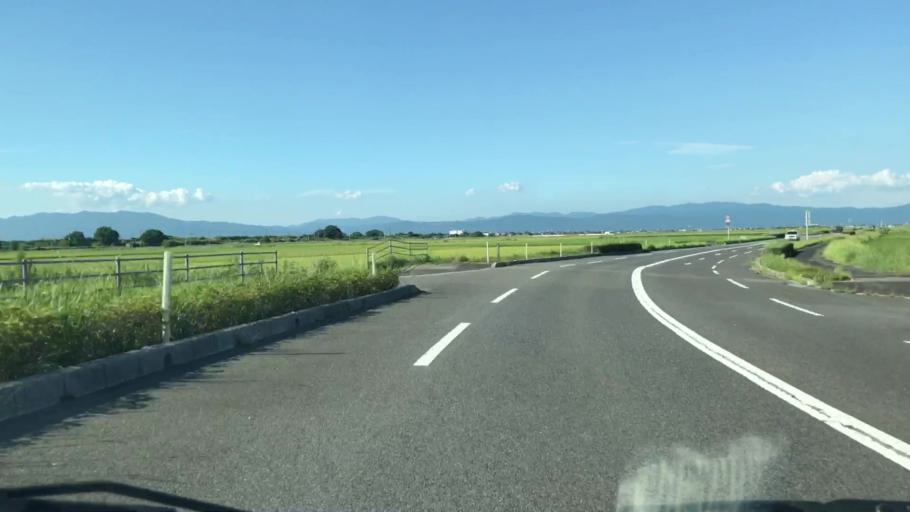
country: JP
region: Saga Prefecture
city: Okawa
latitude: 33.1612
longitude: 130.2900
